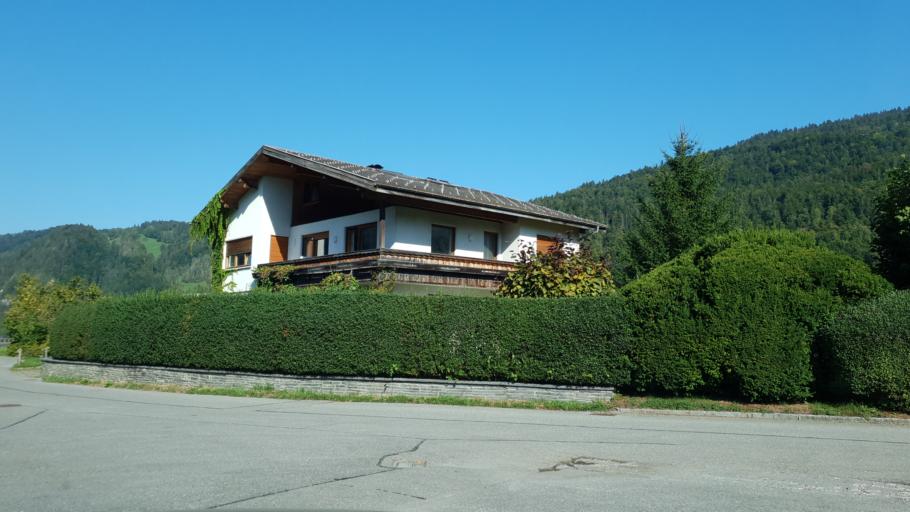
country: AT
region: Vorarlberg
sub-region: Politischer Bezirk Bregenz
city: Bezau
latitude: 47.3824
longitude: 9.8965
